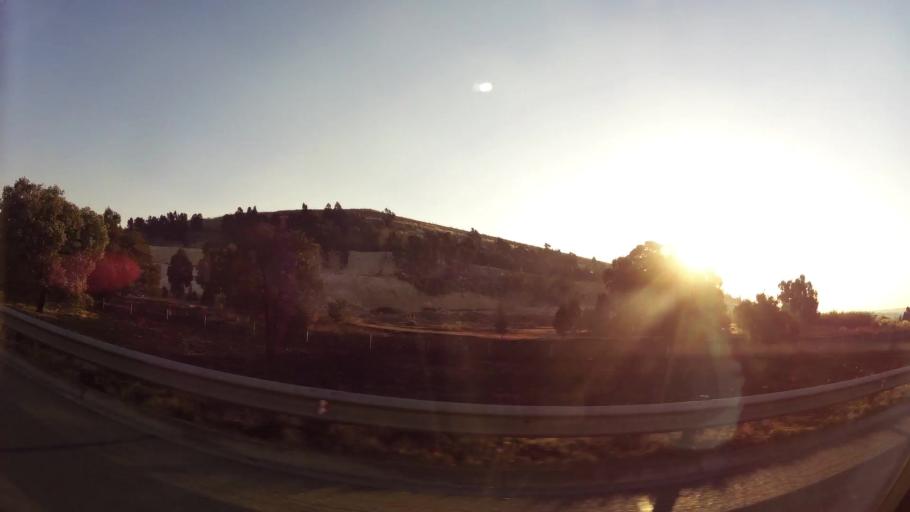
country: ZA
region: Gauteng
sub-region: City of Johannesburg Metropolitan Municipality
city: Johannesburg
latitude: -26.2258
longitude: 27.9613
